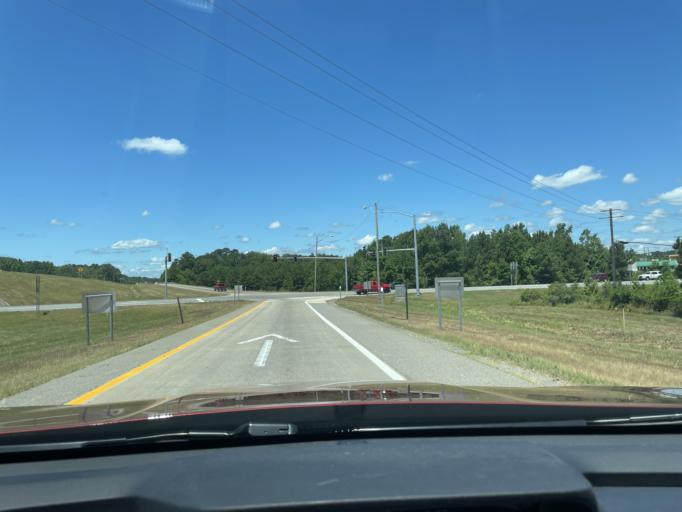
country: US
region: Arkansas
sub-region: Jefferson County
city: Pine Bluff
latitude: 34.1717
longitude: -92.0057
